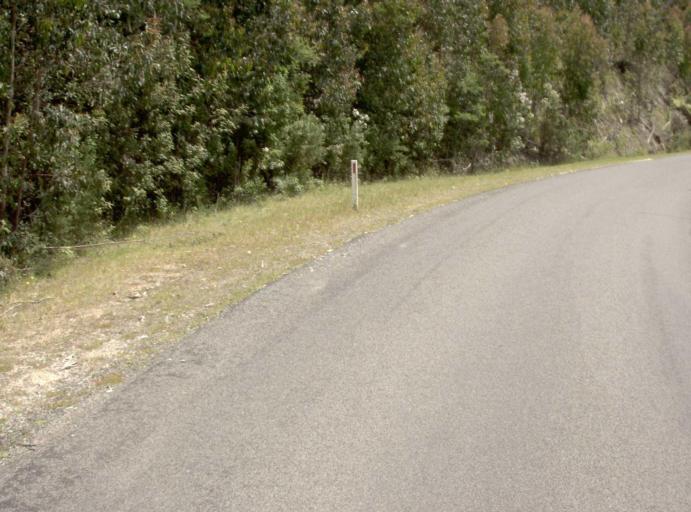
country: AU
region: Victoria
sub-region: Latrobe
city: Traralgon
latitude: -38.4309
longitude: 146.5521
